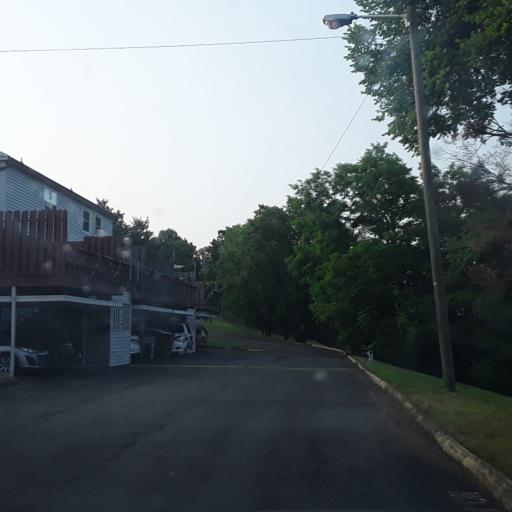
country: US
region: Tennessee
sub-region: Williamson County
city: Brentwood Estates
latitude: 36.0513
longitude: -86.7295
